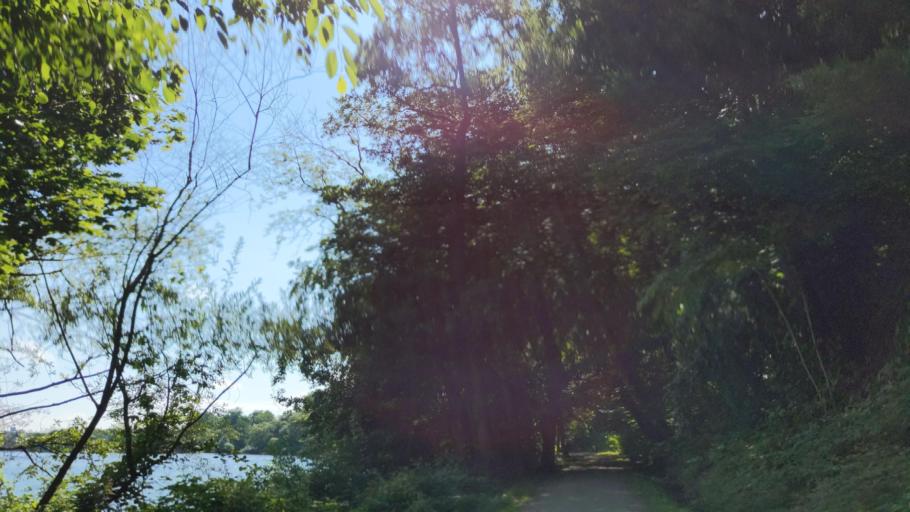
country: DE
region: Schleswig-Holstein
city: Romnitz
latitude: 53.7012
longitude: 10.7550
